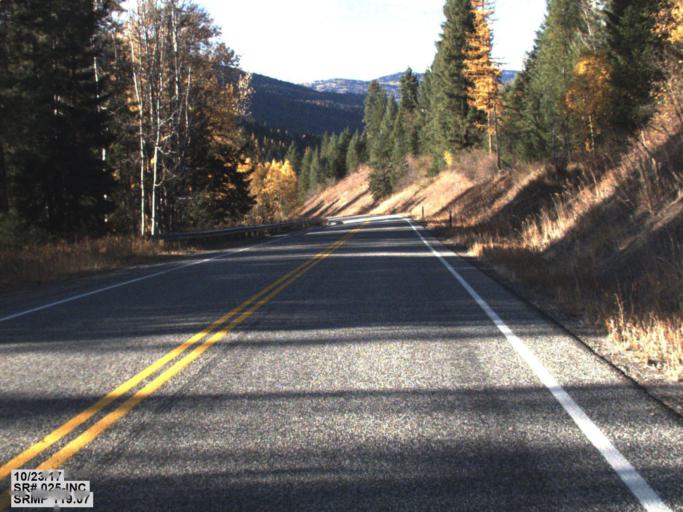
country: CA
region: British Columbia
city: Rossland
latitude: 48.9725
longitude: -117.8154
